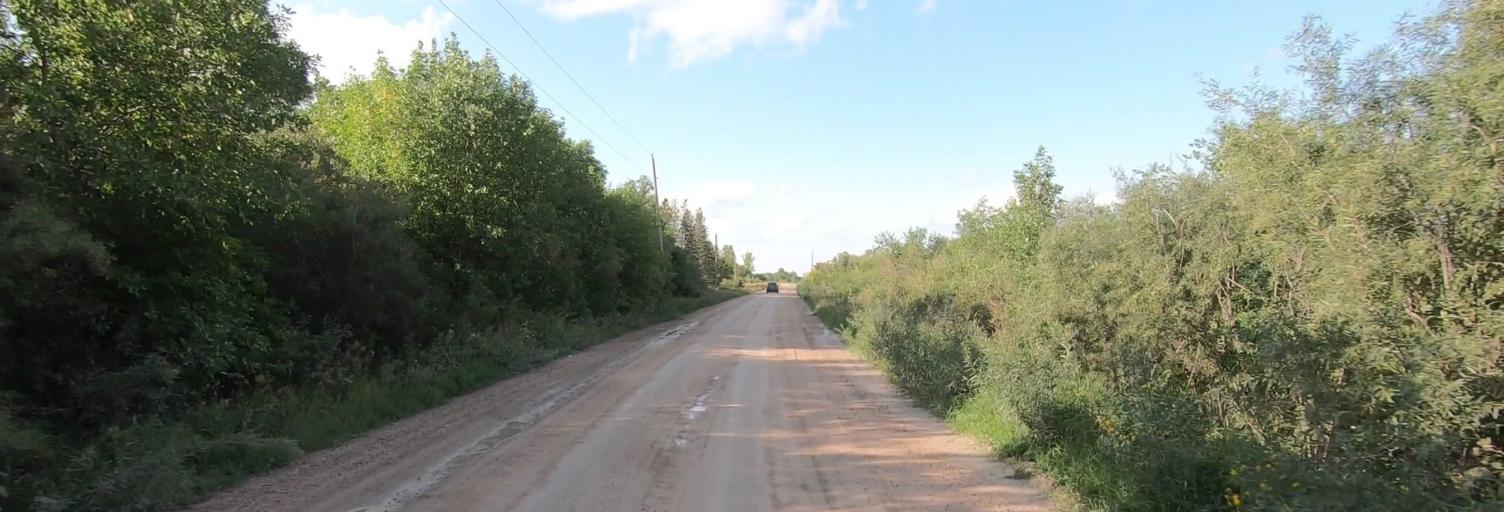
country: CA
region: Manitoba
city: Selkirk
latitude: 50.2525
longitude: -96.8483
